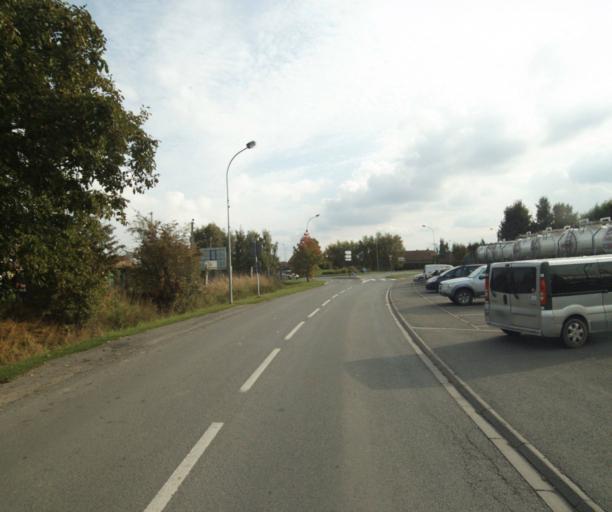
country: FR
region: Nord-Pas-de-Calais
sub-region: Departement du Nord
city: Santes
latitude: 50.6010
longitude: 2.9629
